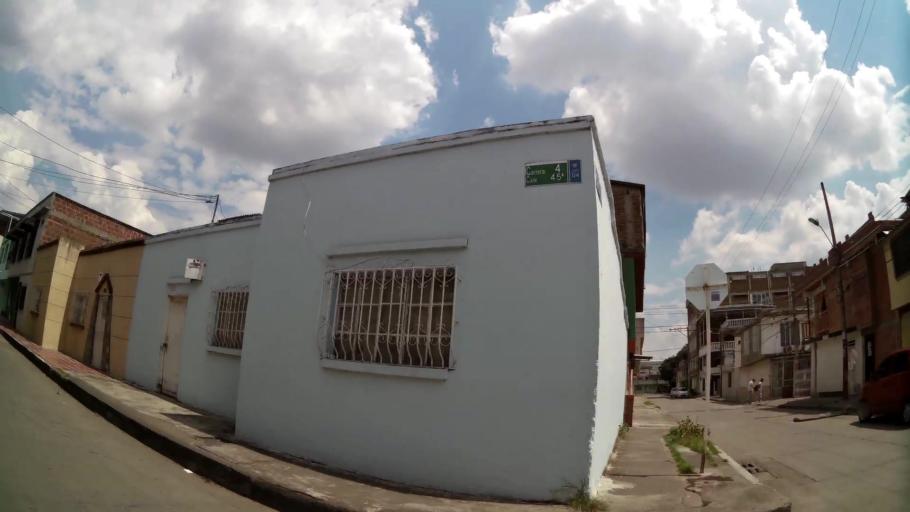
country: CO
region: Valle del Cauca
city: Cali
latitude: 3.4629
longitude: -76.5051
